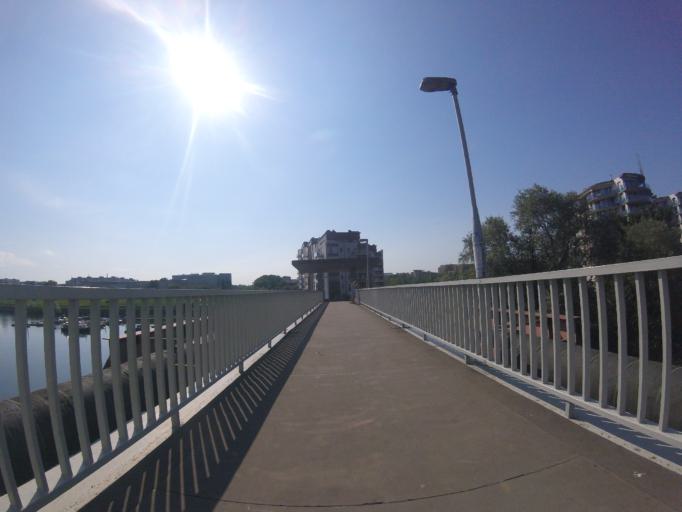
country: HU
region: Budapest
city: Budapest III. keruelet
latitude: 47.5501
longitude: 19.0661
